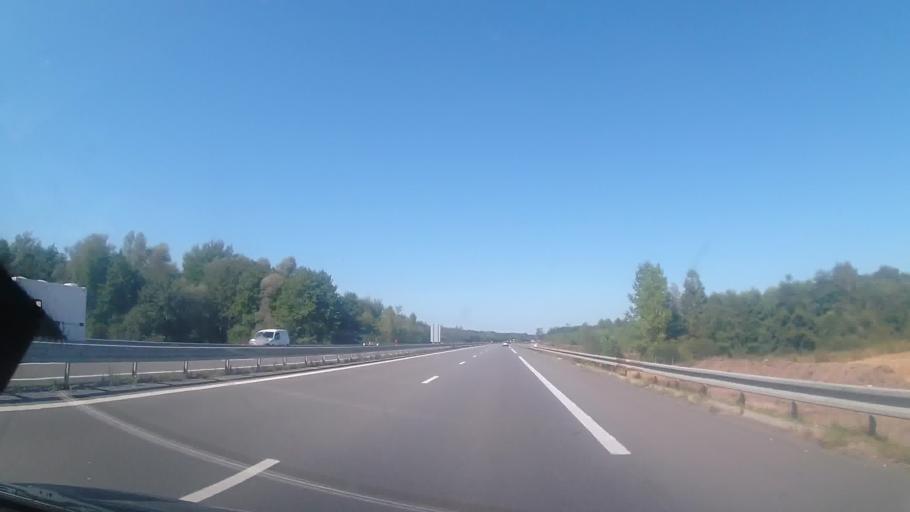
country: FR
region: Centre
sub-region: Departement du Loir-et-Cher
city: Theillay
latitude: 47.3302
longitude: 2.0483
